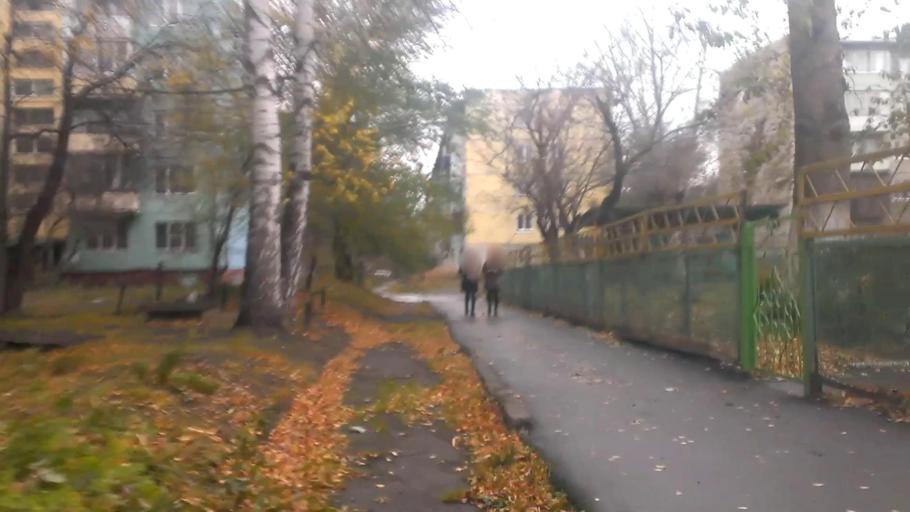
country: RU
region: Altai Krai
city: Novosilikatnyy
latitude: 53.3525
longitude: 83.6866
